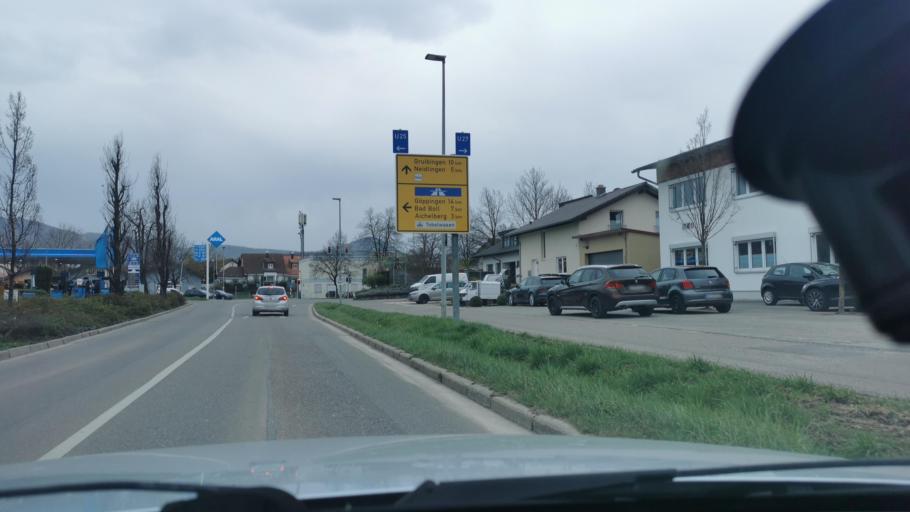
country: DE
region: Baden-Wuerttemberg
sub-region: Regierungsbezirk Stuttgart
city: Weilheim an der Teck
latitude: 48.6208
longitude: 9.5392
